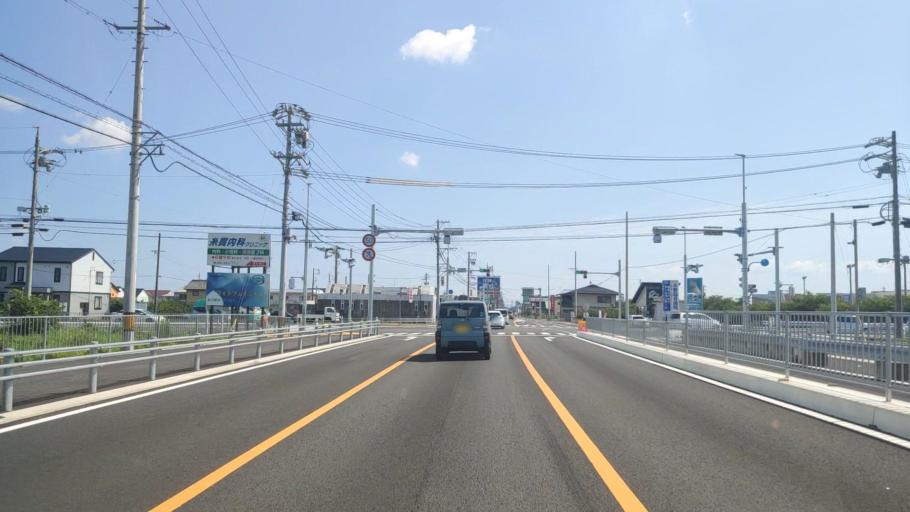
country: JP
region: Gifu
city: Godo
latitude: 35.4590
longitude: 136.6762
